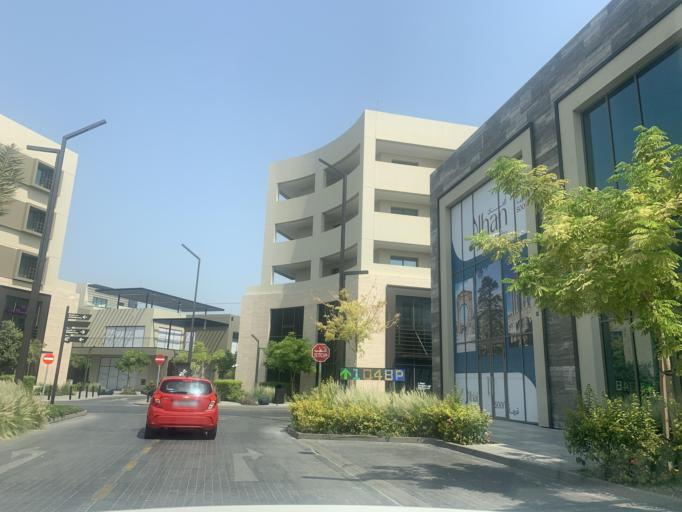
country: BH
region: Central Governorate
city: Madinat Hamad
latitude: 26.1612
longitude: 50.4704
